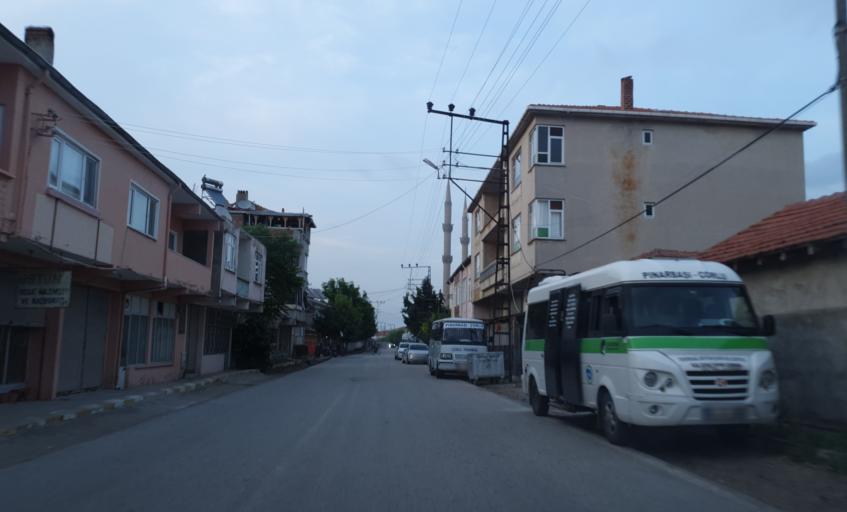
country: TR
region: Tekirdag
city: Beyazkoy
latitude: 41.3830
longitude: 27.6181
